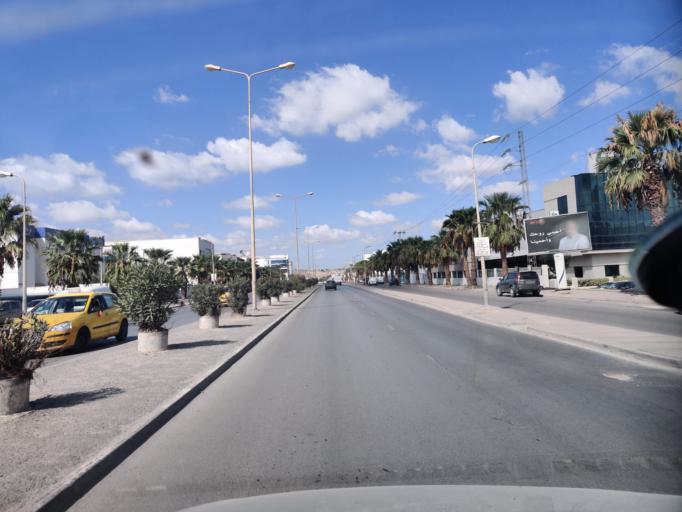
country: TN
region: Bin 'Arus
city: Ben Arous
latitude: 36.7744
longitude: 10.2184
